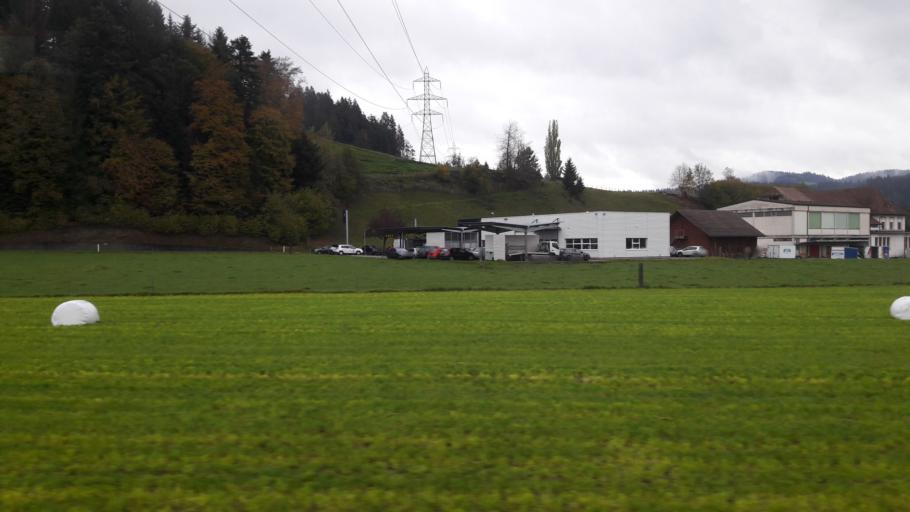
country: CH
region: Bern
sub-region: Emmental District
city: Lutzelfluh
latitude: 47.0018
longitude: 7.7103
